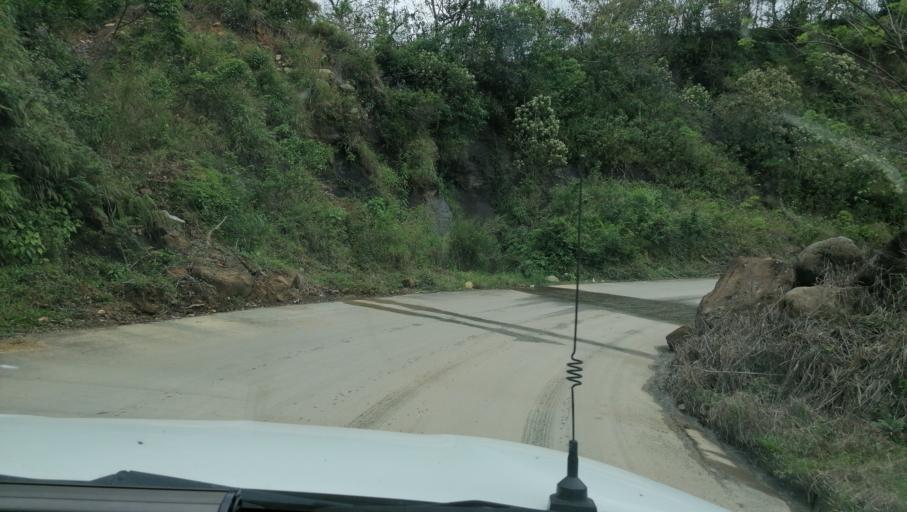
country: MX
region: Chiapas
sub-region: Francisco Leon
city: San Miguel la Sardina
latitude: 17.2707
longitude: -93.2663
